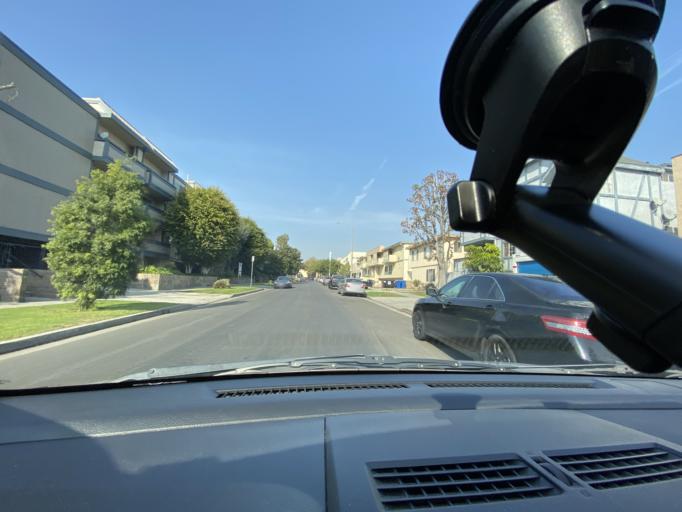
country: US
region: California
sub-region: Los Angeles County
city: Culver City
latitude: 34.0266
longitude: -118.3960
